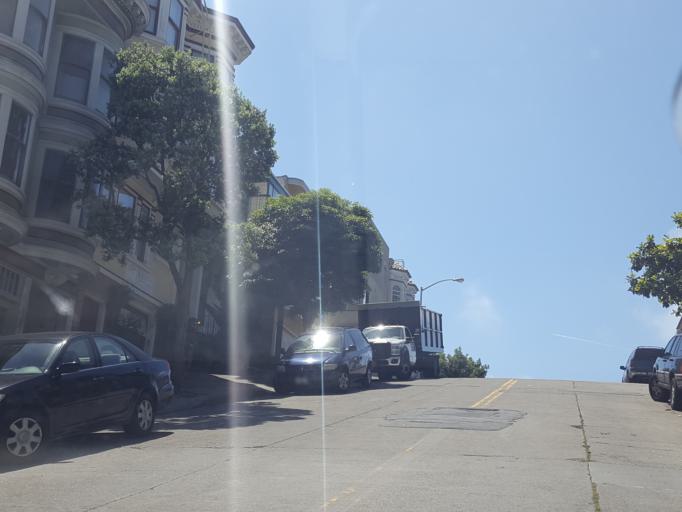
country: US
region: California
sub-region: San Francisco County
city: San Francisco
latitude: 37.8001
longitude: -122.4044
